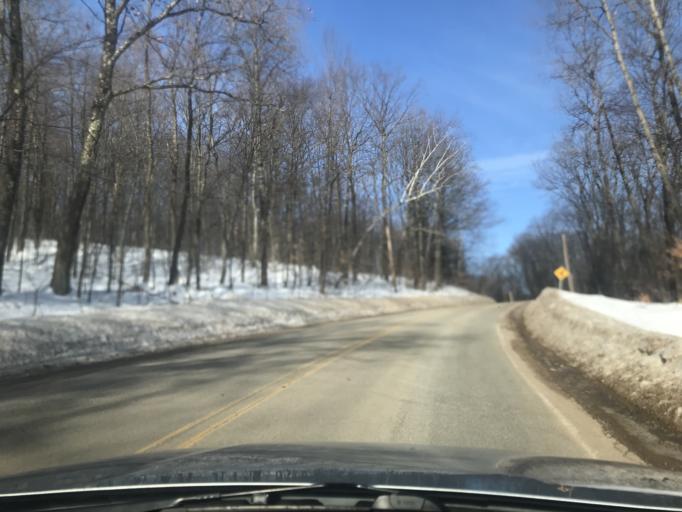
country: US
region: Michigan
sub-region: Dickinson County
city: Kingsford
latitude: 45.4044
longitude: -88.3468
